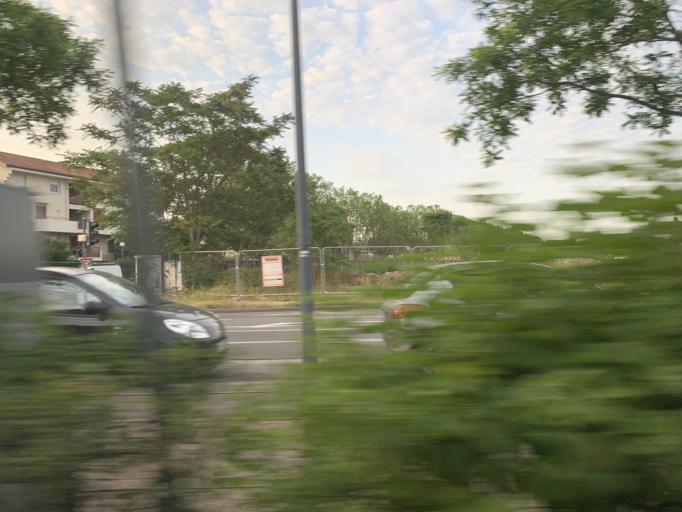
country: FR
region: Rhone-Alpes
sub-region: Departement du Rhone
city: Vaulx-en-Velin
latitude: 45.7627
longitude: 4.9290
